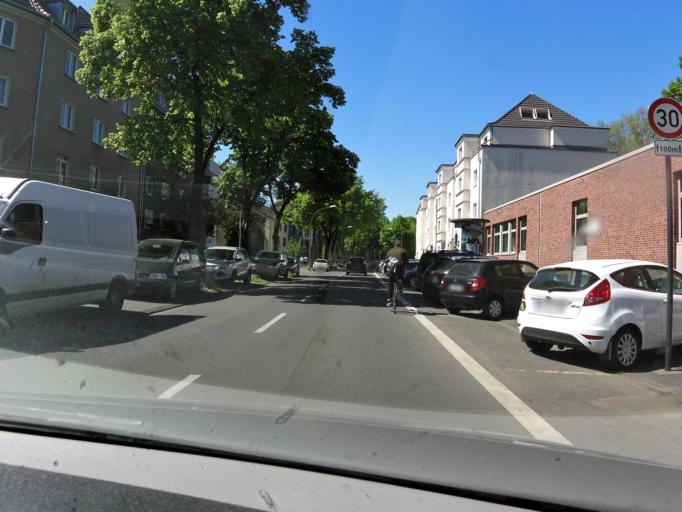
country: DE
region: North Rhine-Westphalia
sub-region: Regierungsbezirk Koln
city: Neustadt/Sued
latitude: 50.9175
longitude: 6.9152
